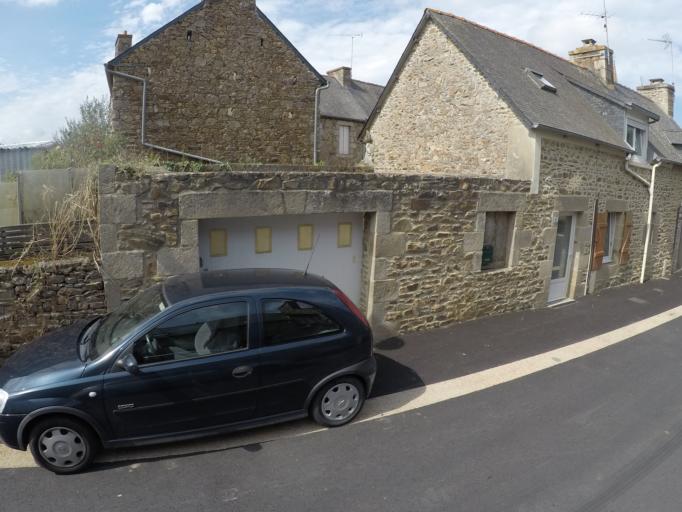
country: FR
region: Brittany
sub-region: Departement des Cotes-d'Armor
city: Goudelin
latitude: 48.6031
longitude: -3.0188
